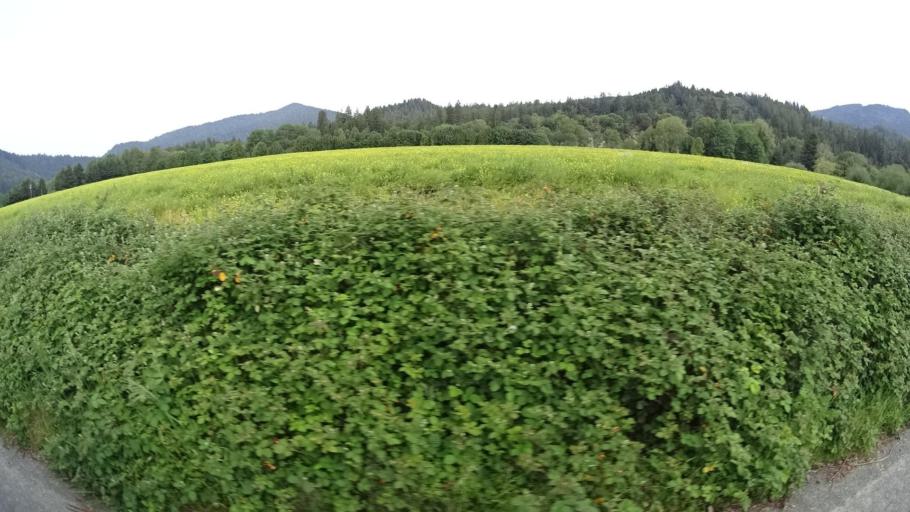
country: US
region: California
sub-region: Humboldt County
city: Redway
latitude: 40.3416
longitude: -123.8933
